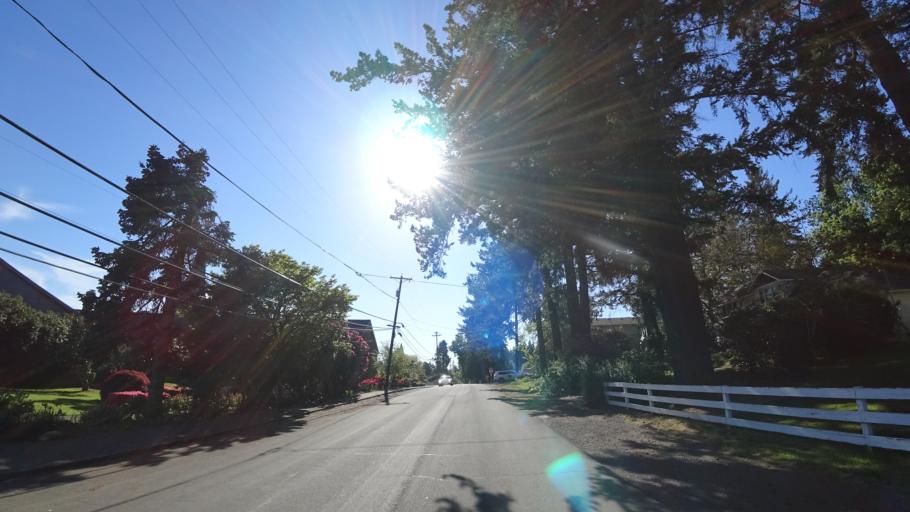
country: US
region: Oregon
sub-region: Washington County
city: West Slope
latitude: 45.4911
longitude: -122.7597
